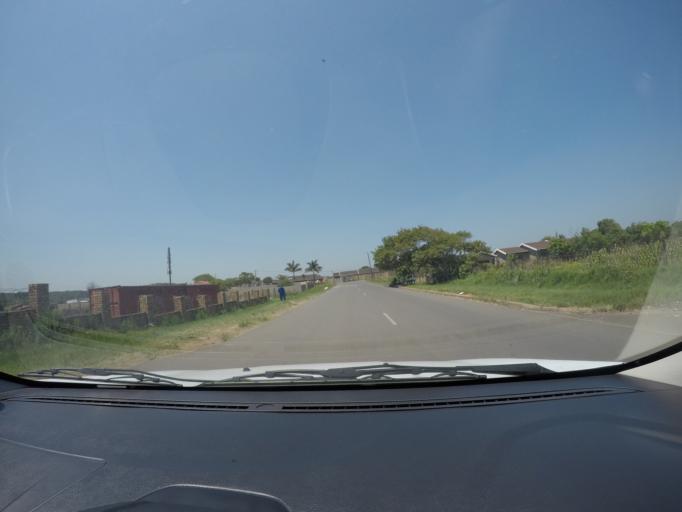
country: ZA
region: KwaZulu-Natal
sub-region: uThungulu District Municipality
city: eSikhawini
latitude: -28.8661
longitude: 31.9098
